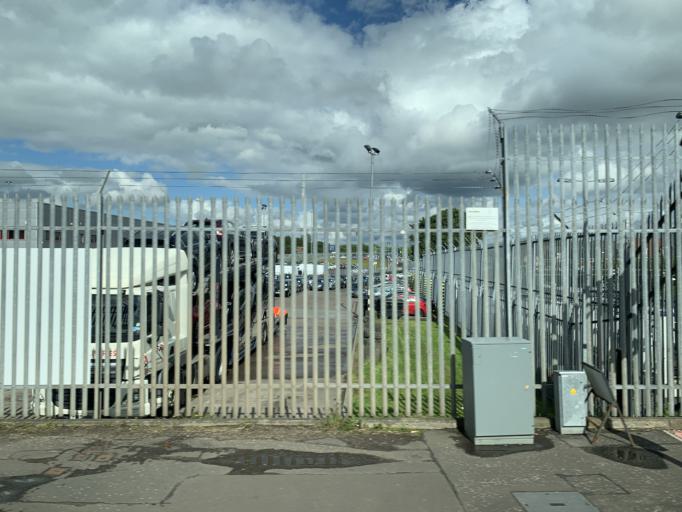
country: GB
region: Scotland
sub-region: North Lanarkshire
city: Chryston
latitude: 55.8600
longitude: -4.1076
